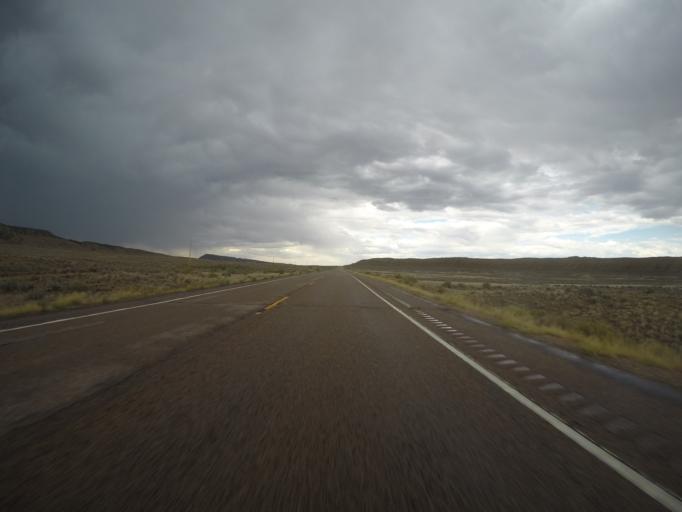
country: US
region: Colorado
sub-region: Rio Blanco County
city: Rangely
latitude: 40.2515
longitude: -108.8431
